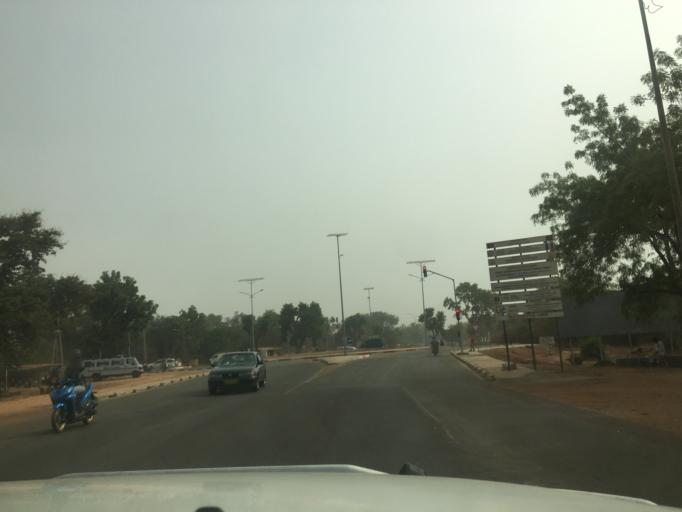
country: BF
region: Centre
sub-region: Kadiogo Province
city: Ouagadougou
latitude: 12.3958
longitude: -1.4985
